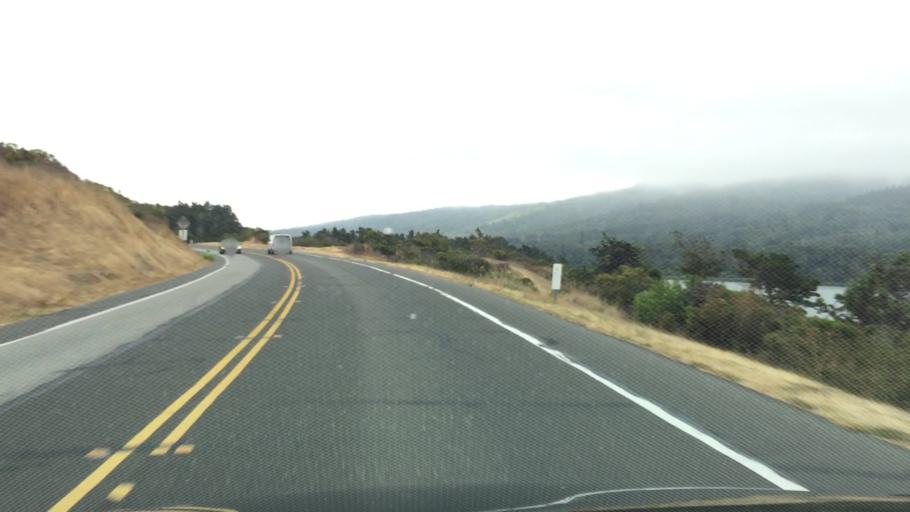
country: US
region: California
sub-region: San Mateo County
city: Highlands-Baywood Park
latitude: 37.4947
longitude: -122.3269
